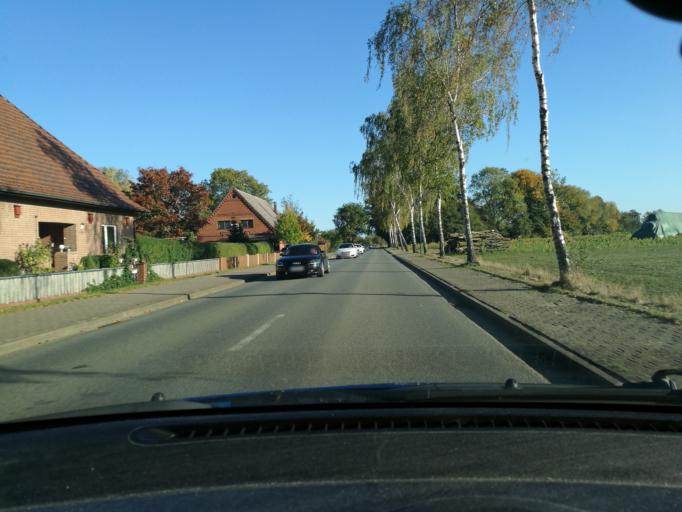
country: DE
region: Lower Saxony
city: Hittbergen
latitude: 53.3202
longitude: 10.6025
